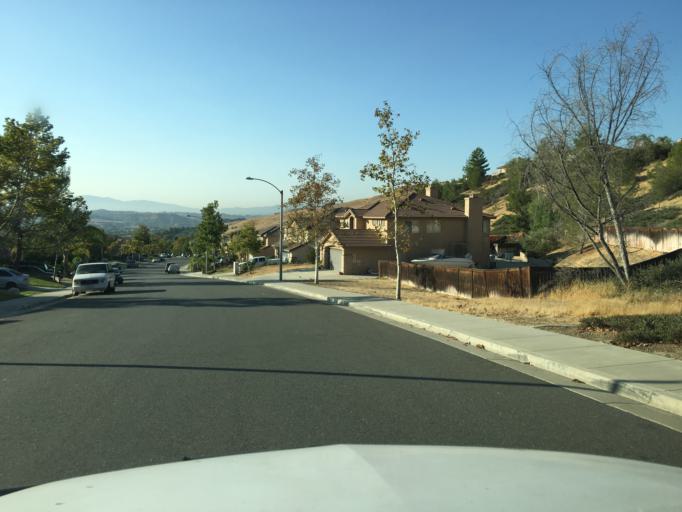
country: US
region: California
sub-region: Los Angeles County
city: Castaic
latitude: 34.5137
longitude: -118.6395
